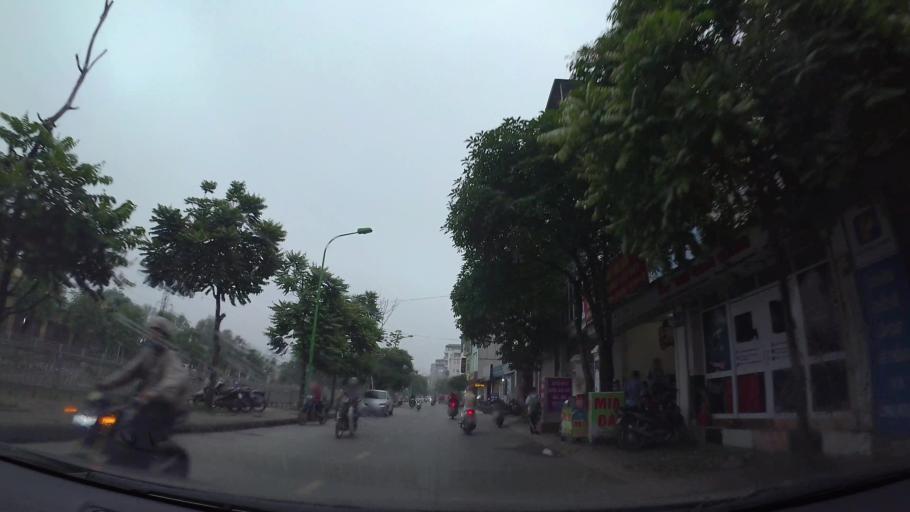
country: VN
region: Ha Noi
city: Hai BaTrung
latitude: 20.9960
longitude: 105.8363
